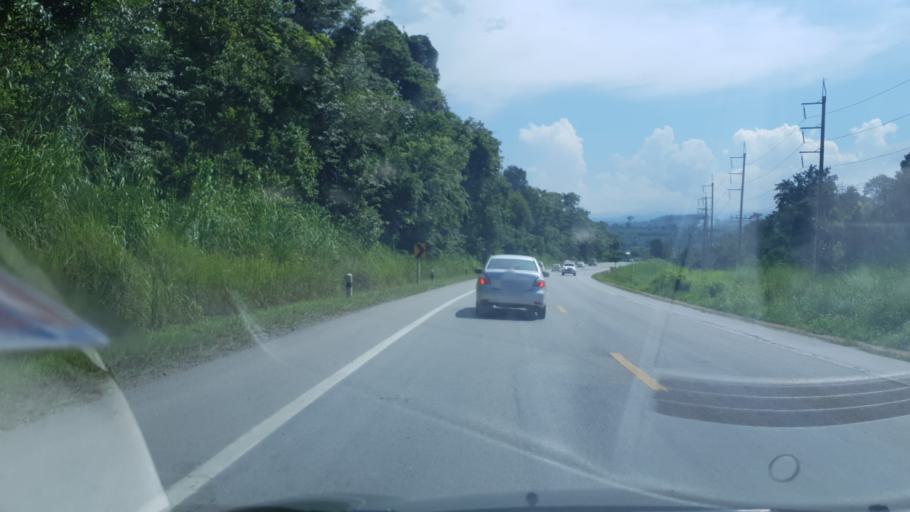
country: TH
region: Chiang Rai
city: Wiang Pa Pao
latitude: 19.4346
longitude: 99.5014
